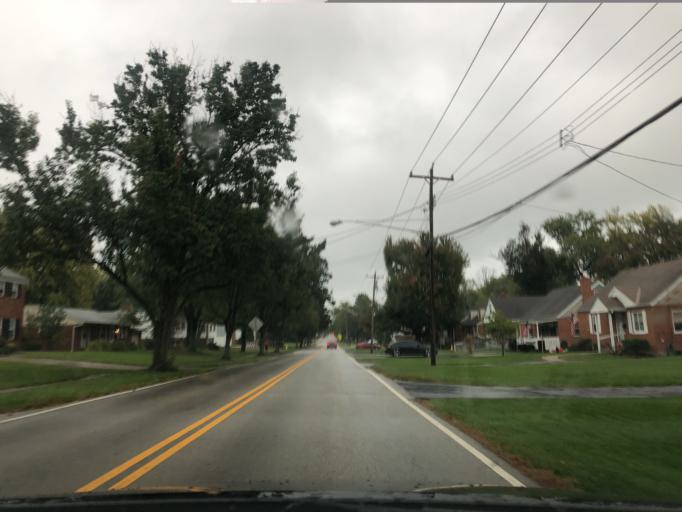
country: US
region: Ohio
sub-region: Hamilton County
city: Blue Ash
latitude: 39.2296
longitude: -84.3867
